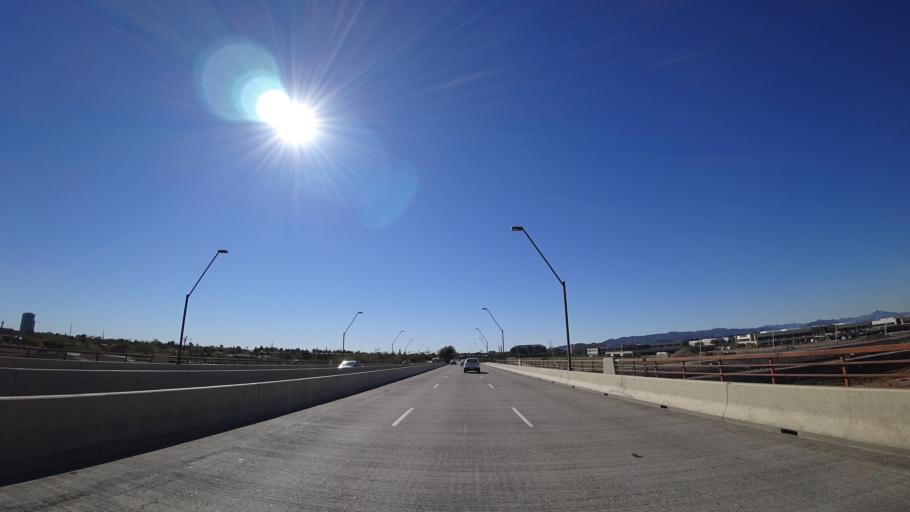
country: US
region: Arizona
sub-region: Maricopa County
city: Tempe Junction
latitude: 33.4350
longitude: -111.9612
